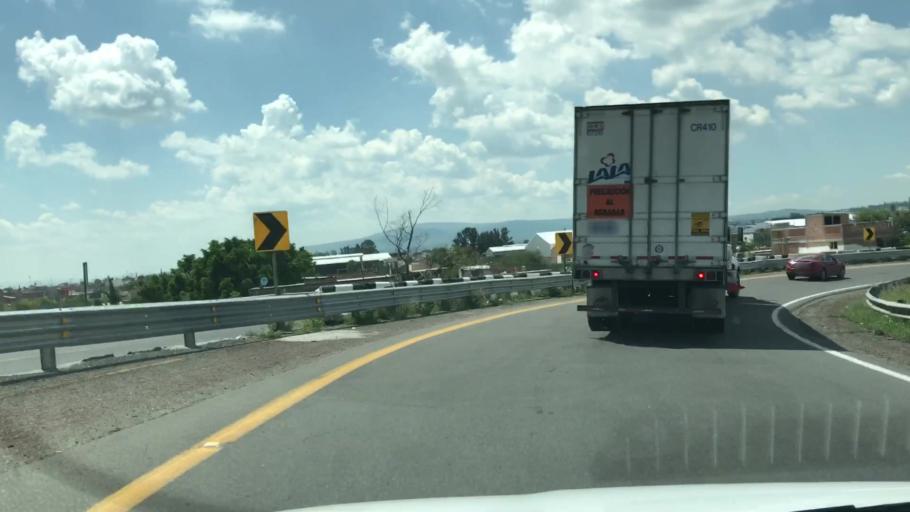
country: MX
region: Guanajuato
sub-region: Irapuato
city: Las Huertas Tercera Seccion
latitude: 20.6498
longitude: -101.3747
